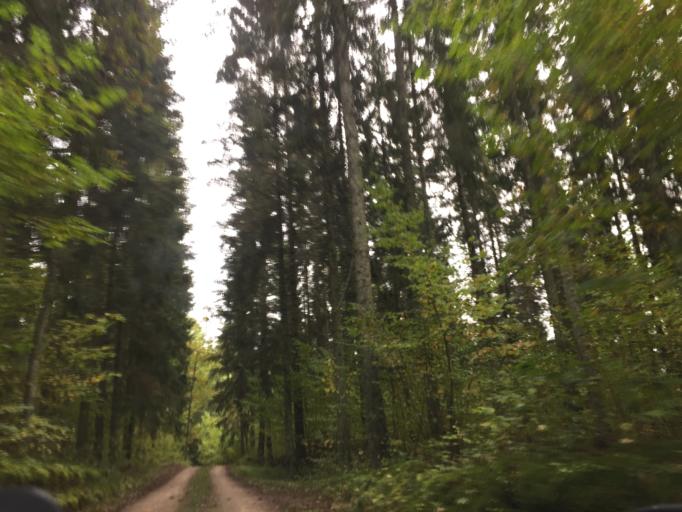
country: LV
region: Auces Novads
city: Auce
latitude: 56.5501
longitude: 23.0335
